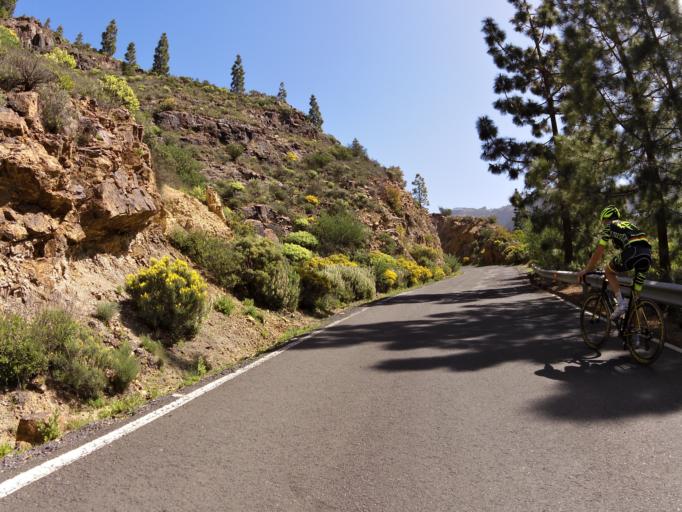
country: ES
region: Canary Islands
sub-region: Provincia de Las Palmas
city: Tejeda
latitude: 27.9536
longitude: -15.6257
